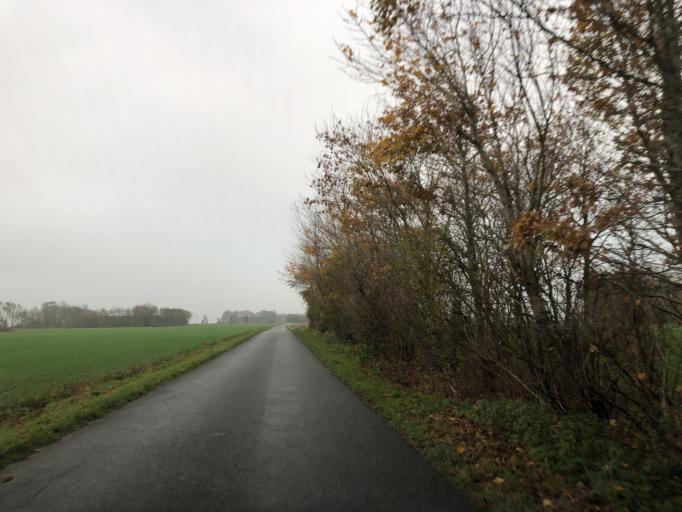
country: DK
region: Central Jutland
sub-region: Herning Kommune
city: Vildbjerg
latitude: 56.2291
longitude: 8.7752
